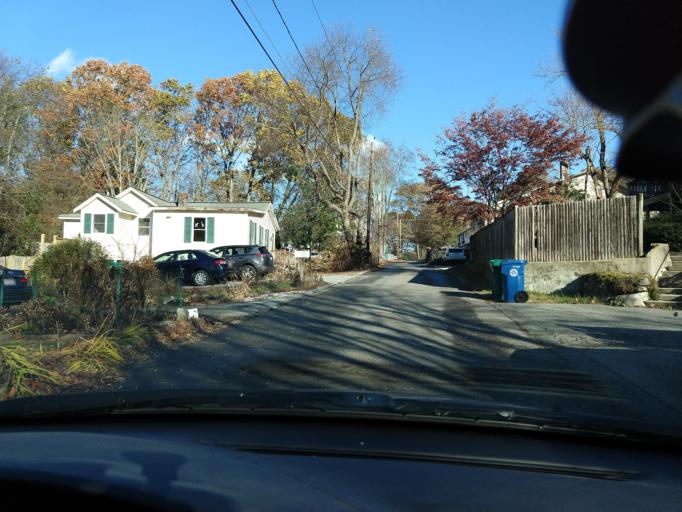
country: US
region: Massachusetts
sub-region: Middlesex County
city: Billerica
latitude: 42.5380
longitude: -71.2606
